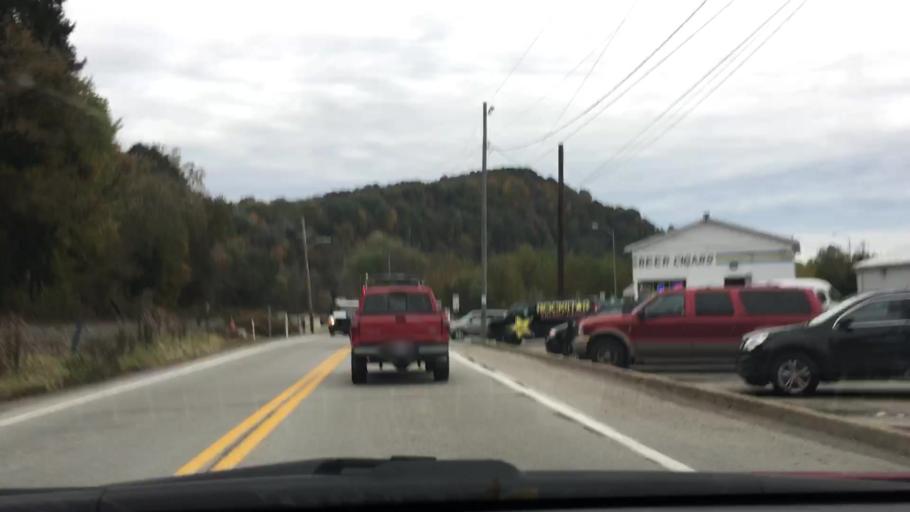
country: US
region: Pennsylvania
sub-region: Armstrong County
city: Apollo
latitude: 40.5788
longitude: -79.5695
